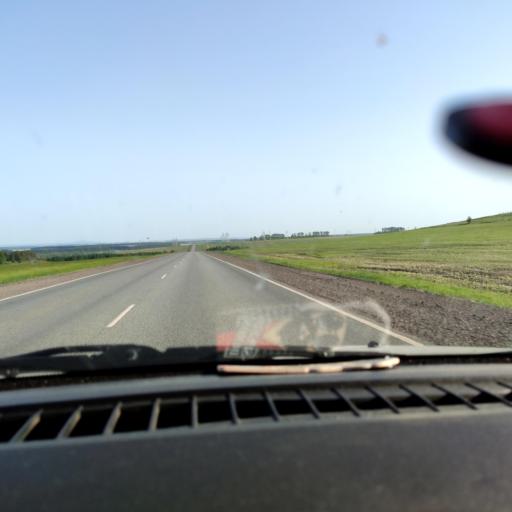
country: RU
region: Bashkortostan
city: Sterlitamak
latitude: 53.5984
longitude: 55.8350
